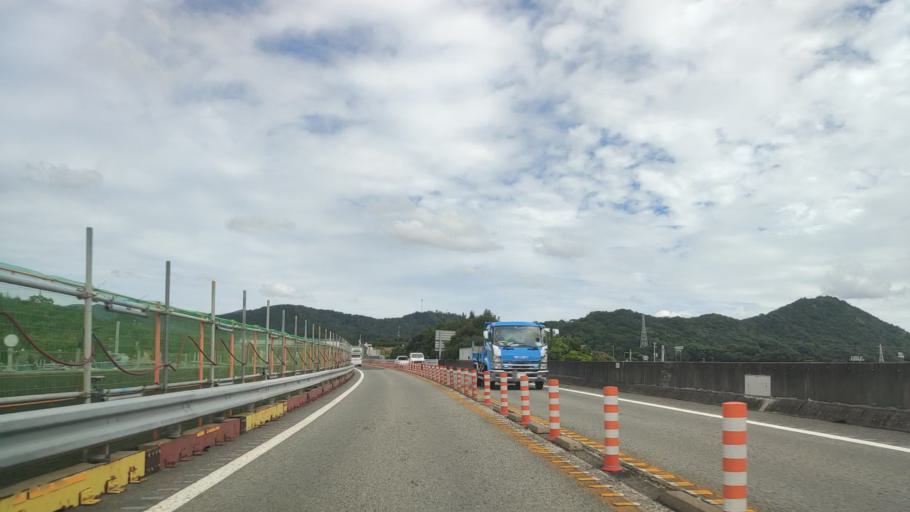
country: JP
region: Wakayama
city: Gobo
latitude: 33.9069
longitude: 135.1932
